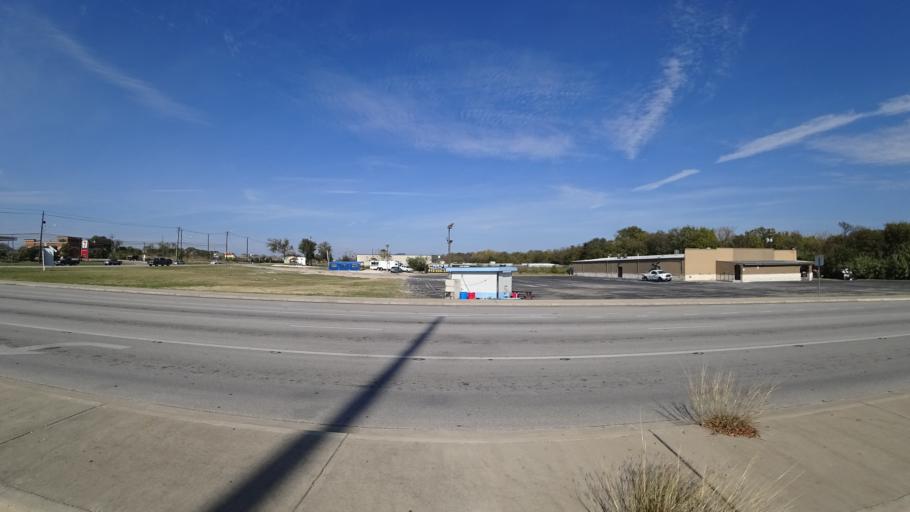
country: US
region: Texas
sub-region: Travis County
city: Pflugerville
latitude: 30.4032
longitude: -97.6377
